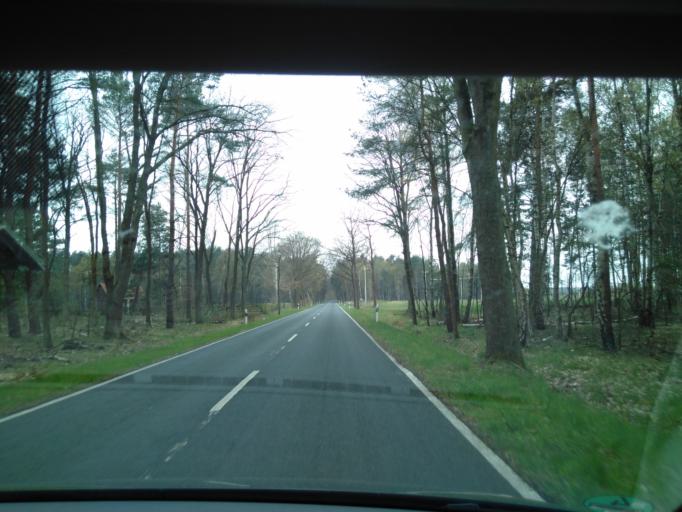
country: DE
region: Lower Saxony
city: Adelheidsdorf
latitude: 52.5947
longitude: 10.0506
